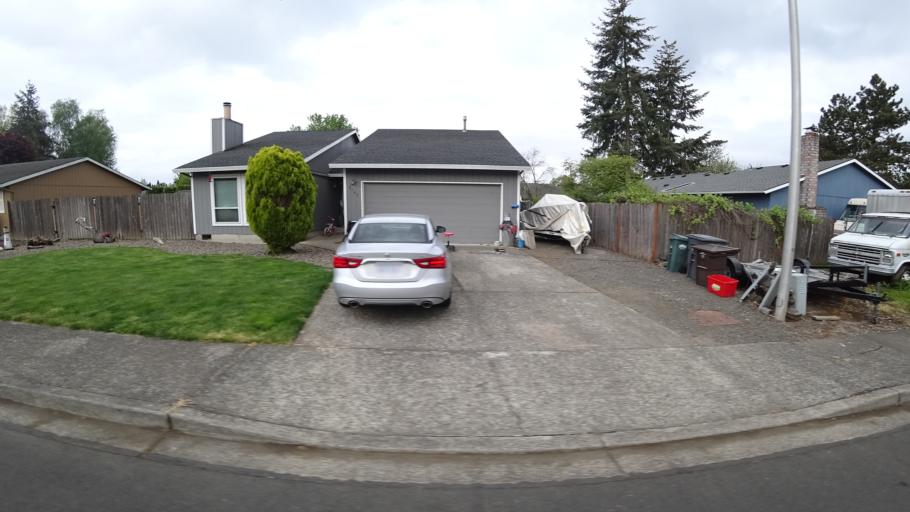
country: US
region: Oregon
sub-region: Washington County
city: Hillsboro
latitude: 45.5399
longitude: -122.9745
